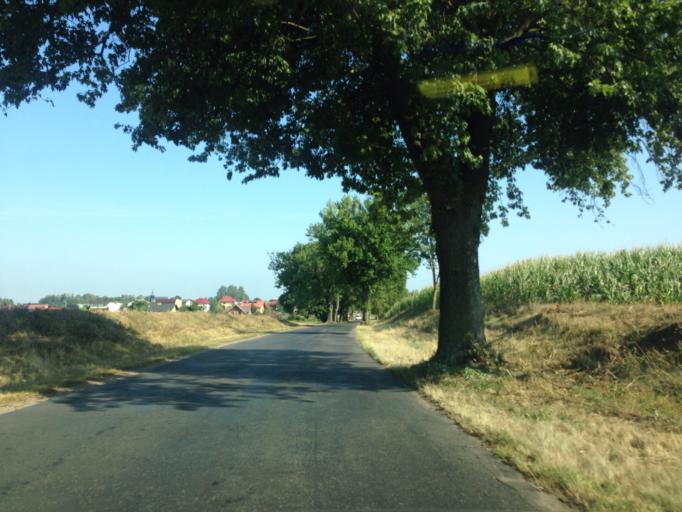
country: PL
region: Kujawsko-Pomorskie
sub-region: Powiat brodnicki
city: Brzozie
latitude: 53.3183
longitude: 19.6065
